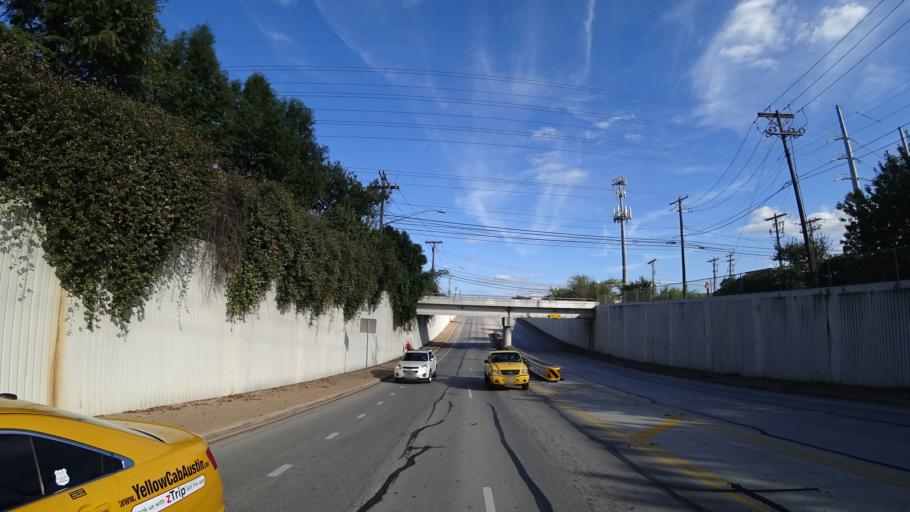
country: US
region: Texas
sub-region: Williamson County
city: Jollyville
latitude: 30.3676
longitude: -97.7412
